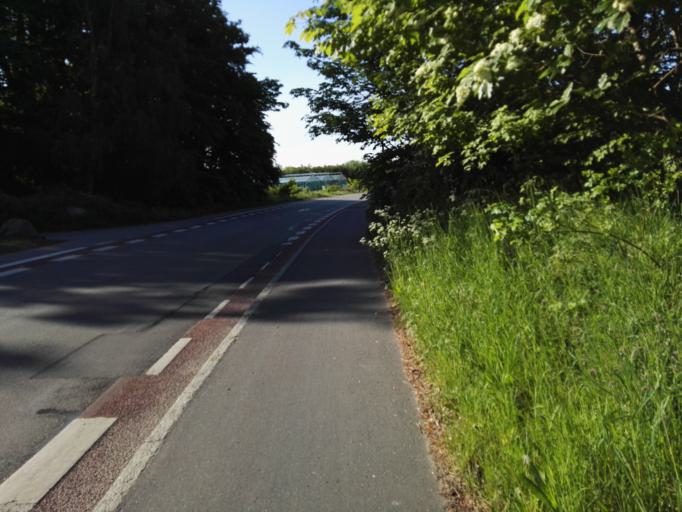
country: DK
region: Capital Region
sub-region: Ballerup Kommune
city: Ballerup
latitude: 55.7450
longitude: 12.3522
